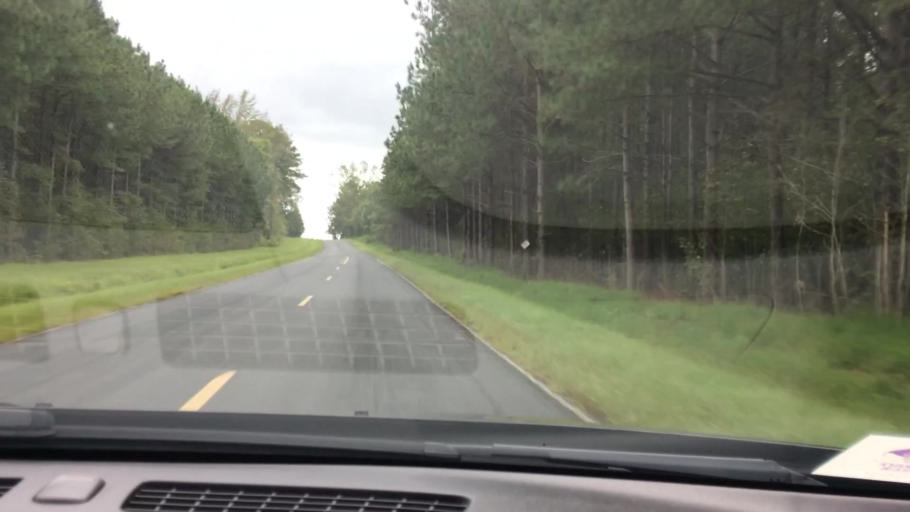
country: US
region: North Carolina
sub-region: Greene County
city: Maury
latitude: 35.5270
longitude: -77.5437
